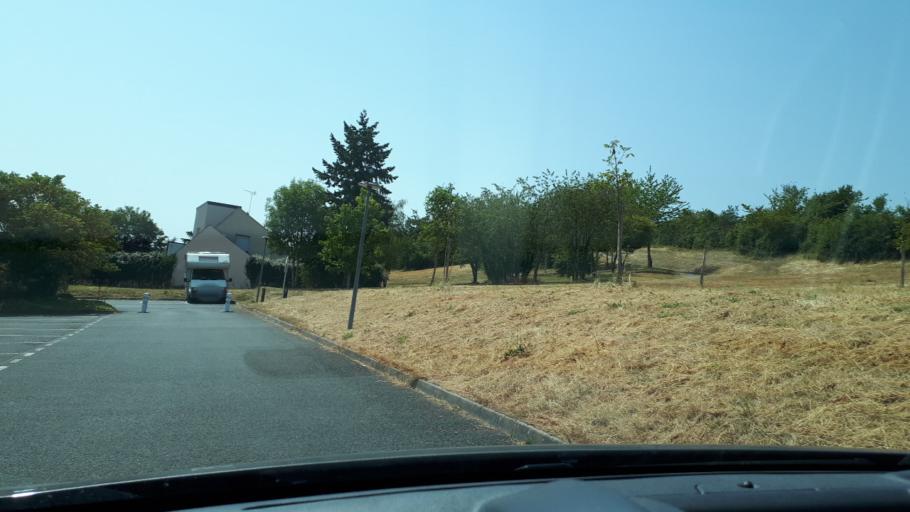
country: FR
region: Centre
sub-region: Departement du Loir-et-Cher
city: Vendome
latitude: 47.8095
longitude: 1.0552
